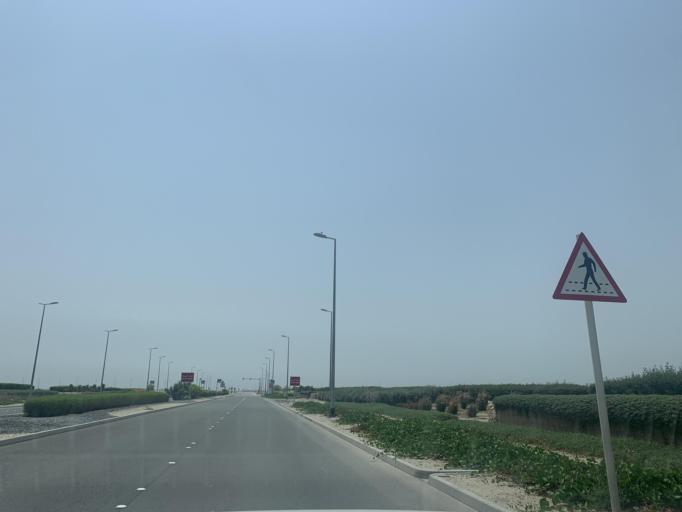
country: BH
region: Central Governorate
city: Dar Kulayb
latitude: 25.8478
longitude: 50.5932
